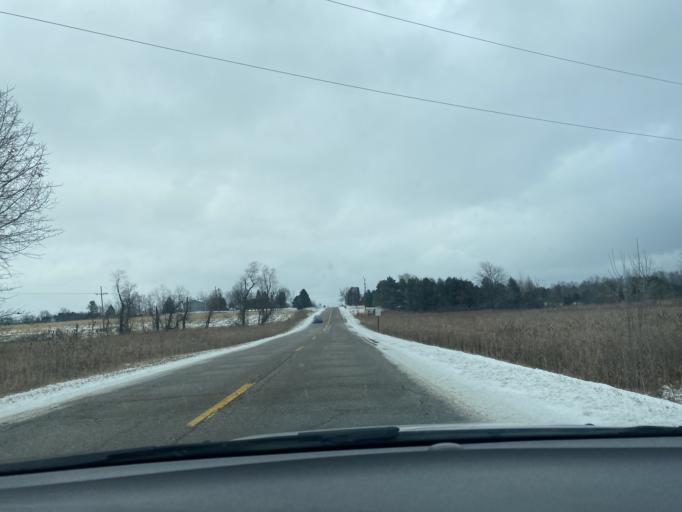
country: US
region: Michigan
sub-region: Lapeer County
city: North Branch
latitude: 43.2084
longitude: -83.1661
